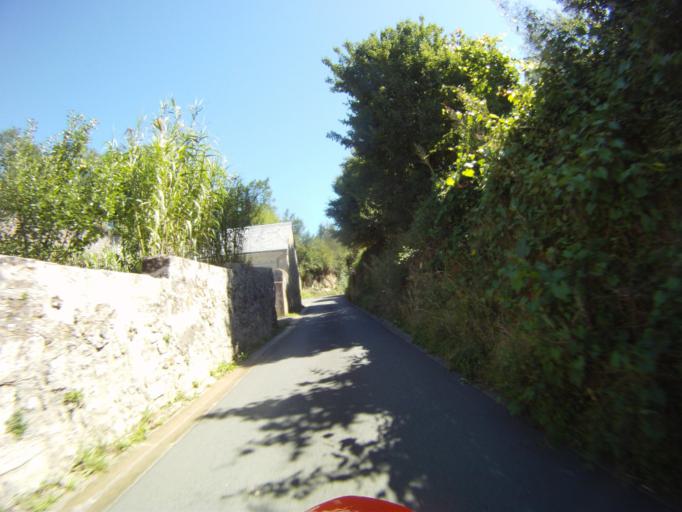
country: FR
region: Centre
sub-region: Departement d'Indre-et-Loire
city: Vouvray
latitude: 47.4398
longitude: 0.7954
